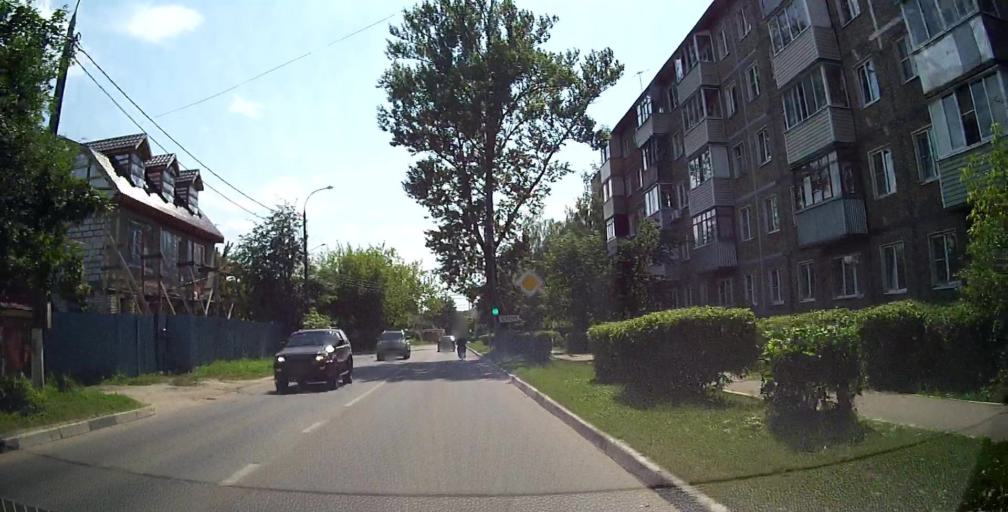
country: RU
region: Moskovskaya
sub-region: Podol'skiy Rayon
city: Podol'sk
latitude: 55.4128
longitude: 37.5259
